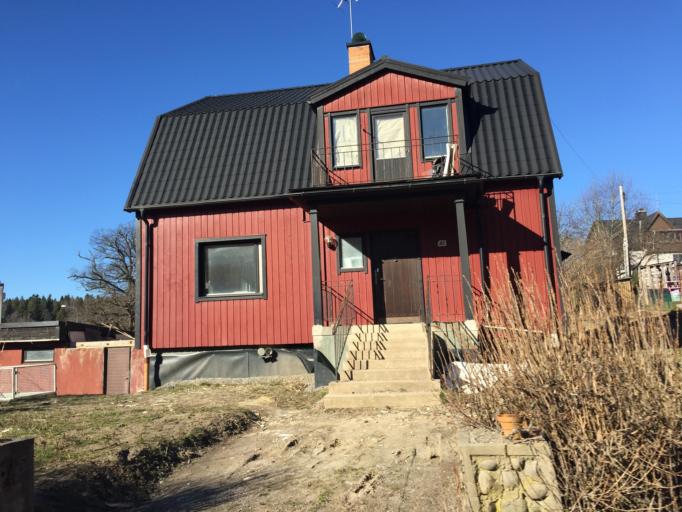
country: SE
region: OEstergoetland
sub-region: Finspangs Kommun
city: Finspang
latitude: 58.7108
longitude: 15.7937
